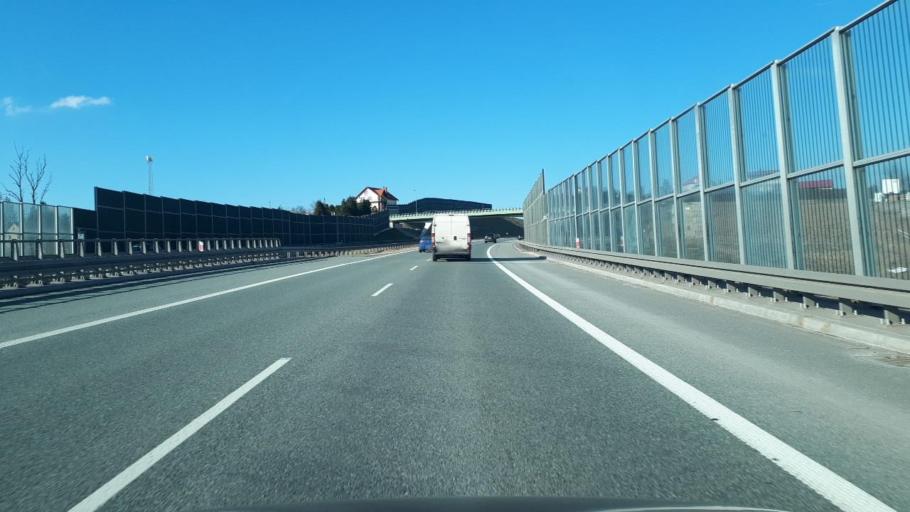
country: PL
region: Silesian Voivodeship
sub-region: Powiat zywiecki
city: Lesna
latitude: 49.6888
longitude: 19.1388
